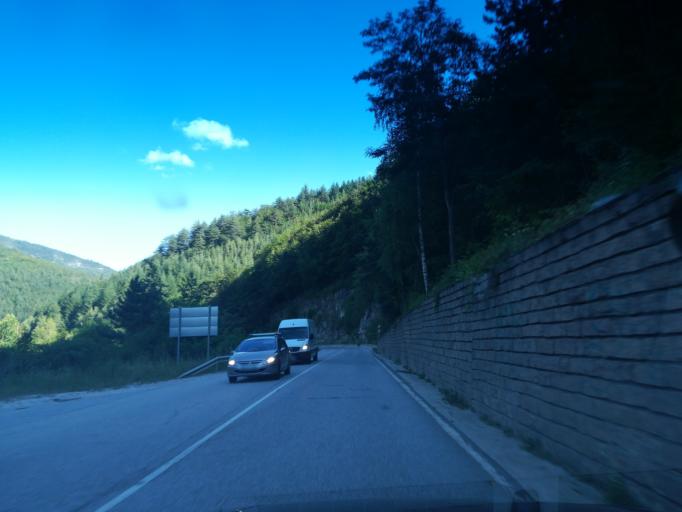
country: BG
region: Smolyan
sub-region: Obshtina Chepelare
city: Chepelare
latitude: 41.8277
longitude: 24.6870
